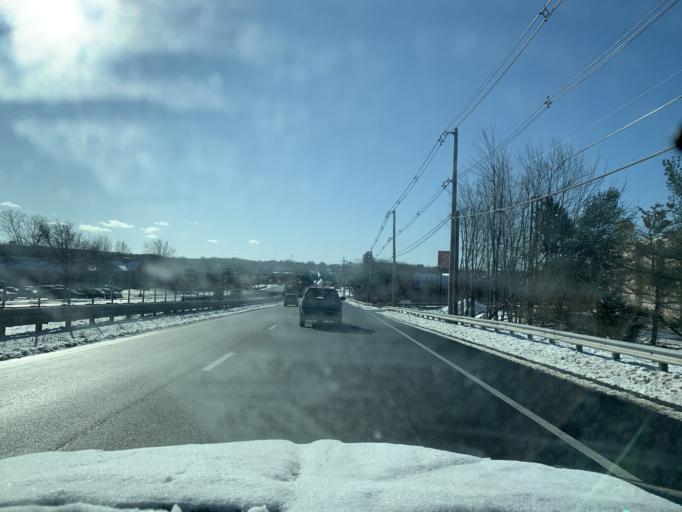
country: US
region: Massachusetts
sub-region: Essex County
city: Danvers
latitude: 42.5641
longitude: -70.9761
